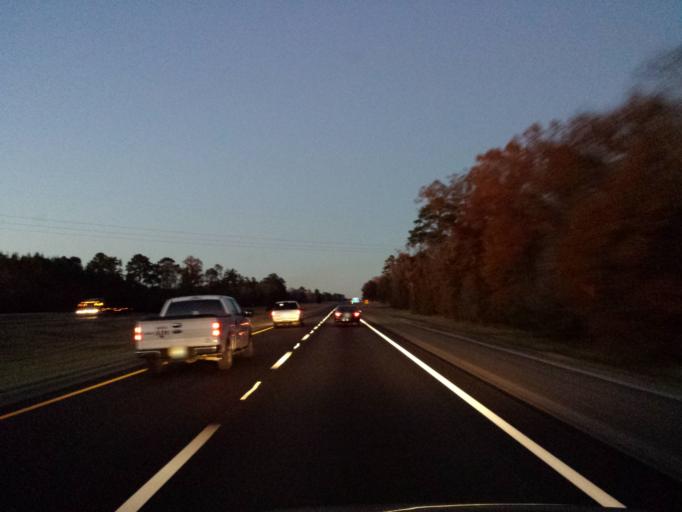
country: US
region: Mississippi
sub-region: Jones County
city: Sharon
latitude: 31.8000
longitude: -89.0539
